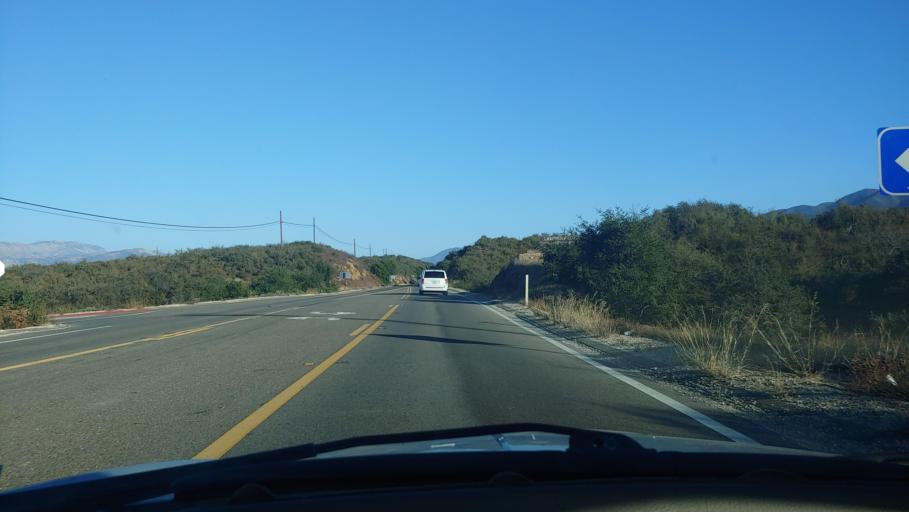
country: US
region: California
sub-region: Santa Barbara County
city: Santa Ynez
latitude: 34.5771
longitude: -119.9781
